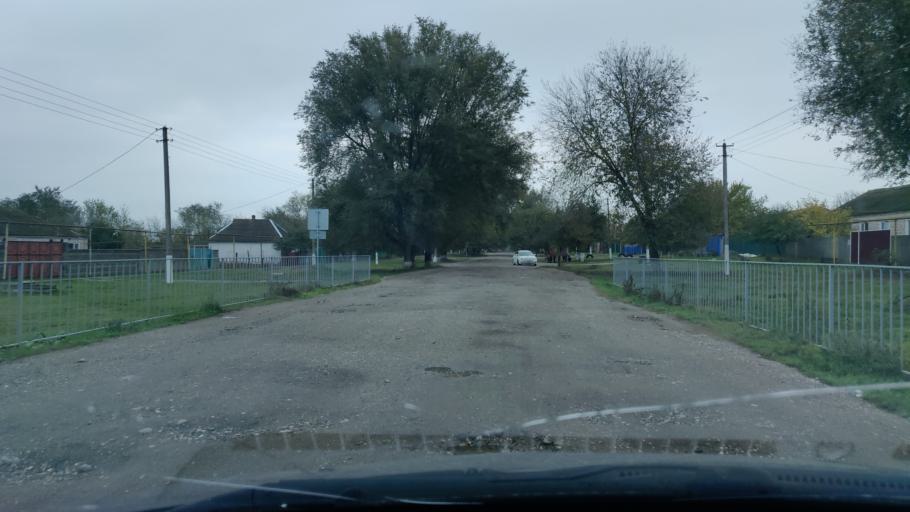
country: RU
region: Stavropol'skiy
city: Irgakly
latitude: 44.2443
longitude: 44.7201
